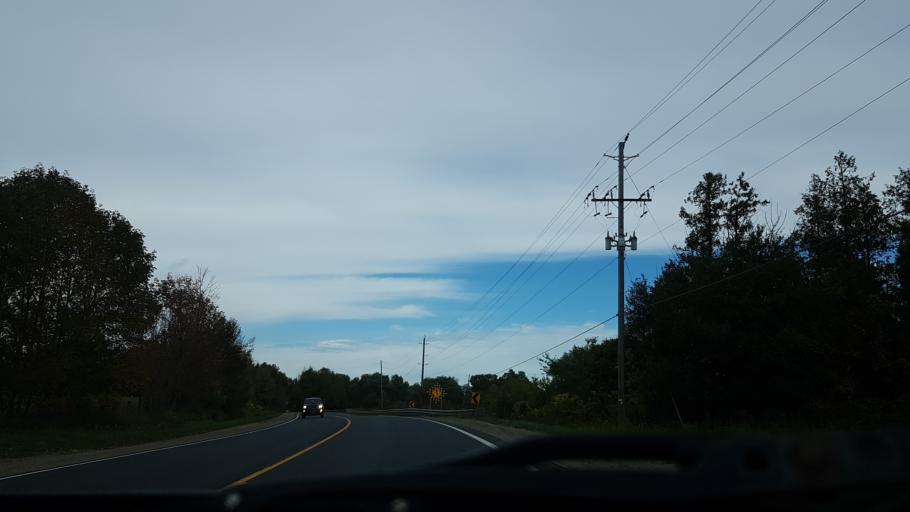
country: CA
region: Ontario
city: Angus
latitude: 44.3045
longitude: -80.0710
